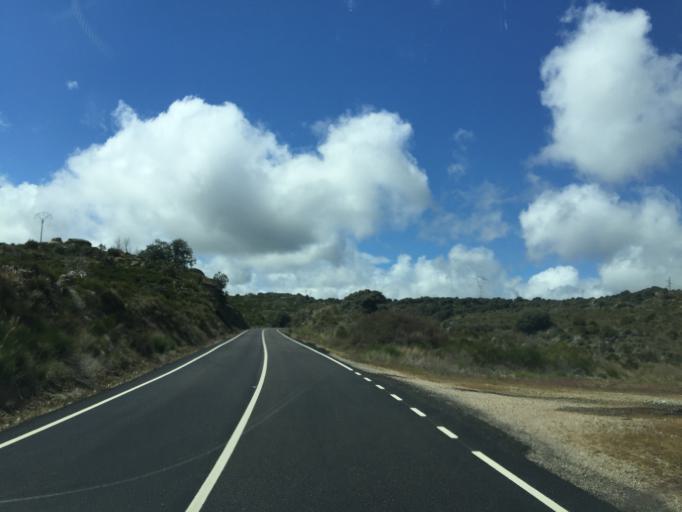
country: ES
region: Castille and Leon
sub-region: Provincia de Zamora
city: Moral de Sayago
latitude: 41.4865
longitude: -6.0891
